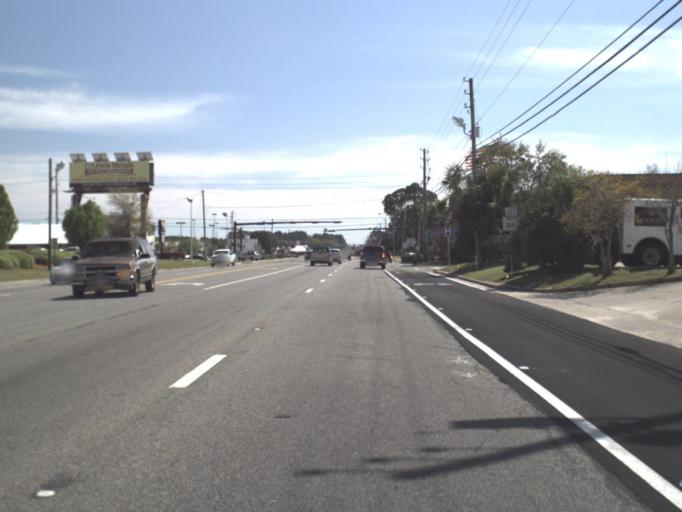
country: US
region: Florida
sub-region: Bay County
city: Hiland Park
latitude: 30.1912
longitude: -85.6500
